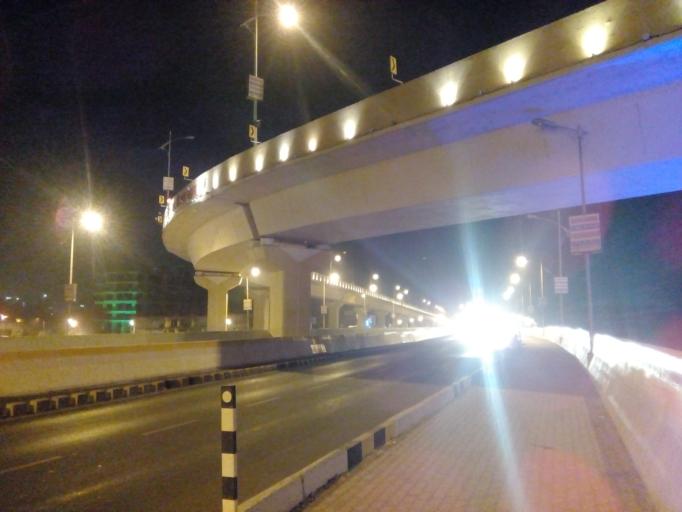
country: IN
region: Maharashtra
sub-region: Pune Division
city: Pimpri
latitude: 18.6067
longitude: 73.8223
